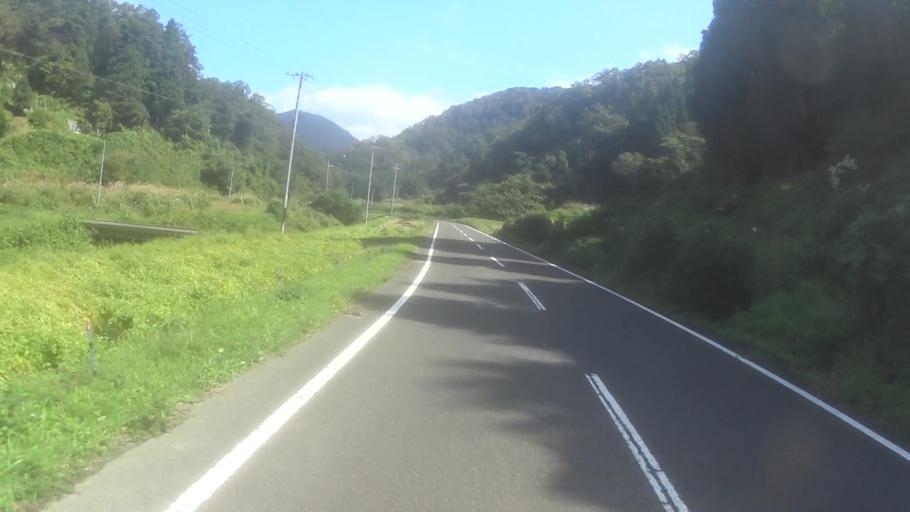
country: JP
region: Kyoto
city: Miyazu
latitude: 35.6749
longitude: 135.1498
